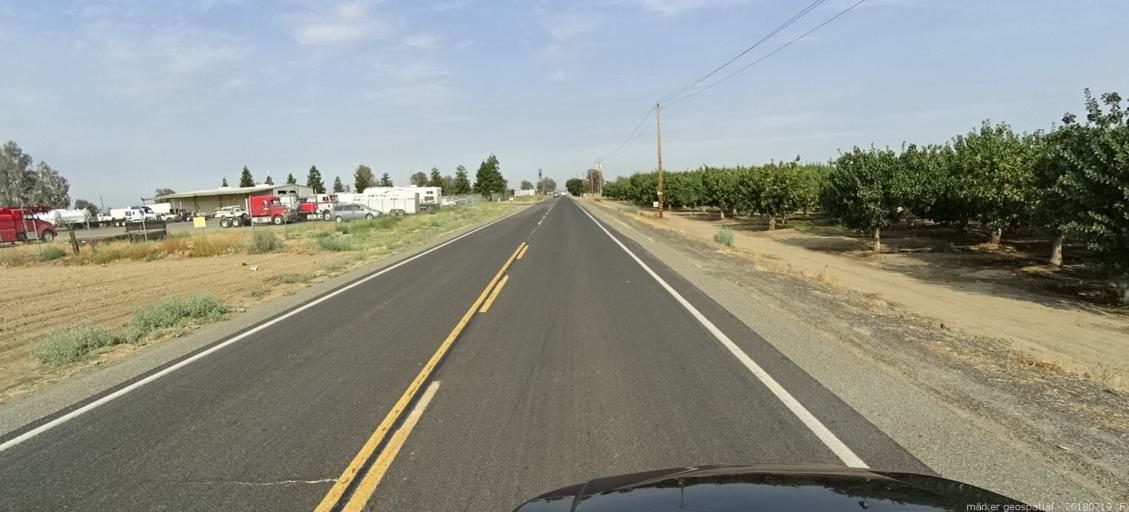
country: US
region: California
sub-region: Madera County
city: Fairmead
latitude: 37.0983
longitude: -120.2116
